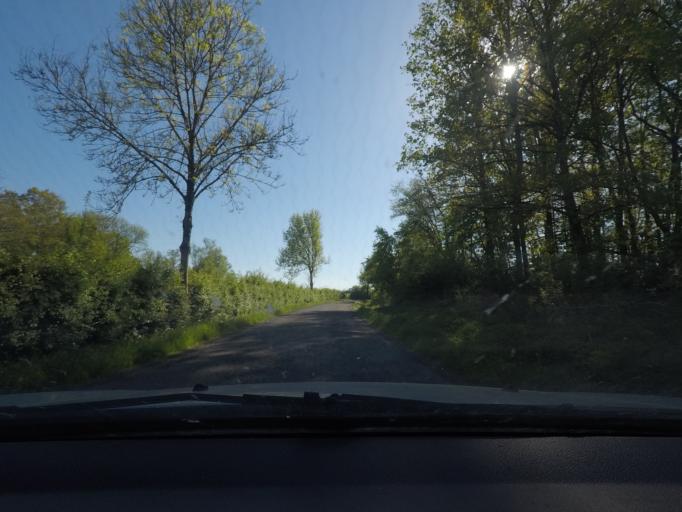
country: BE
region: Wallonia
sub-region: Province du Luxembourg
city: Tintigny
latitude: 49.7122
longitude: 5.4785
